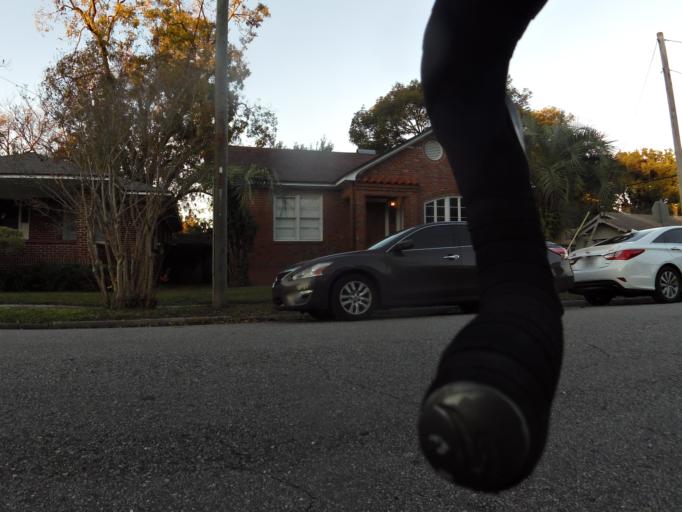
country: US
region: Florida
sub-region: Duval County
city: Jacksonville
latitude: 30.3166
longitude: -81.6957
